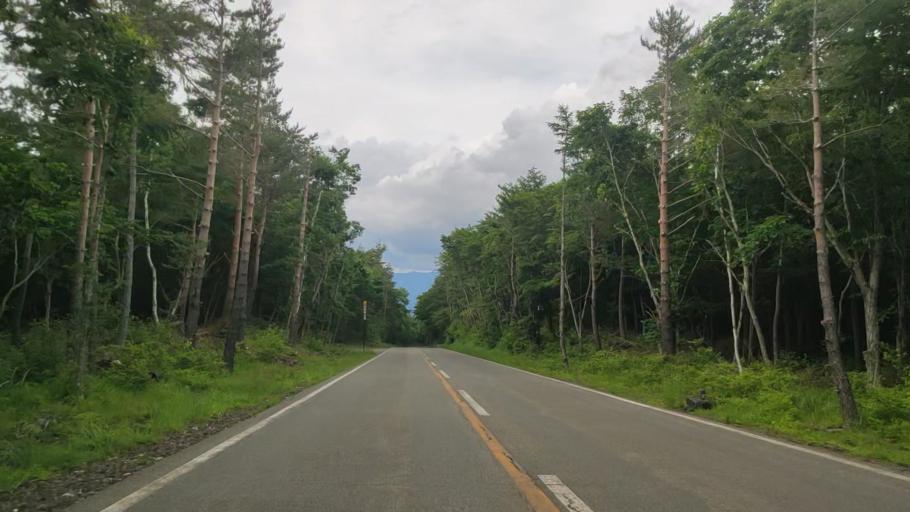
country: JP
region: Yamanashi
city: Fujikawaguchiko
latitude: 35.4396
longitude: 138.7453
